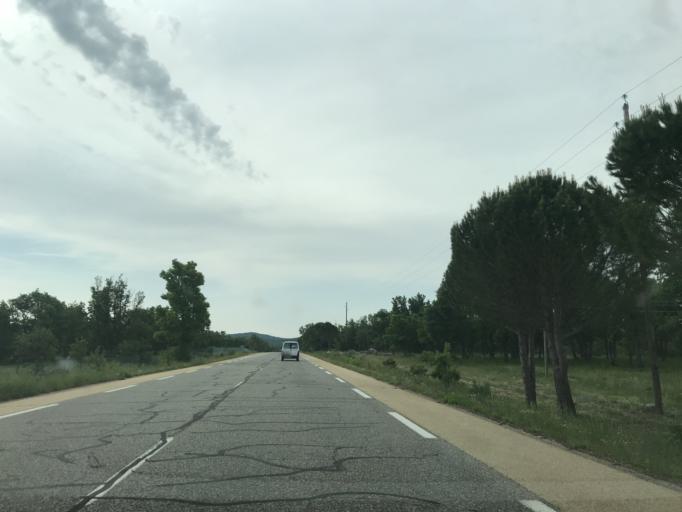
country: FR
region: Provence-Alpes-Cote d'Azur
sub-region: Departement du Var
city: Rians
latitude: 43.5654
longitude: 5.7813
